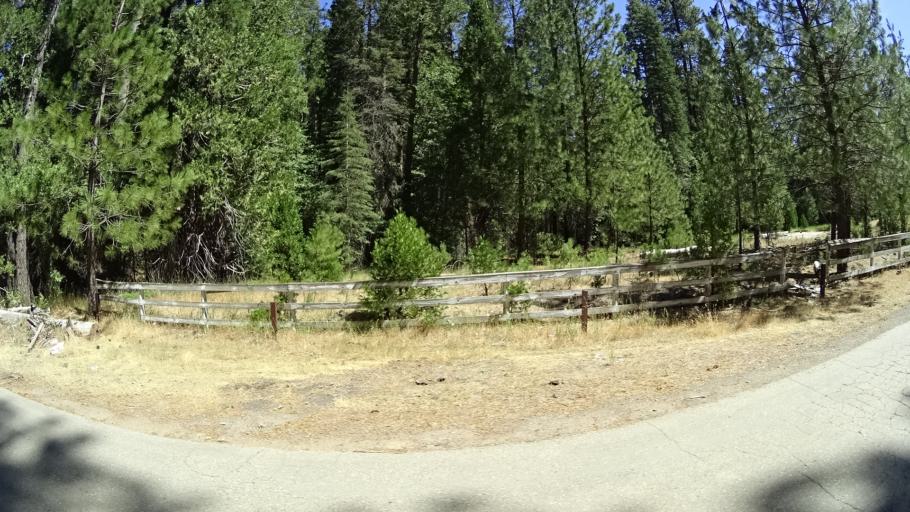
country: US
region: California
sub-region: Amador County
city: Pioneer
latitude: 38.4295
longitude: -120.4511
